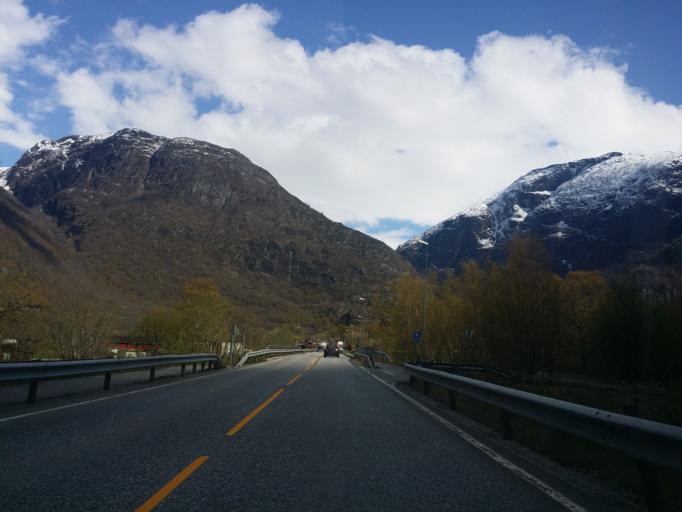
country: NO
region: Hordaland
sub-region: Eidfjord
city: Eidfjord
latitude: 60.4249
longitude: 7.1150
